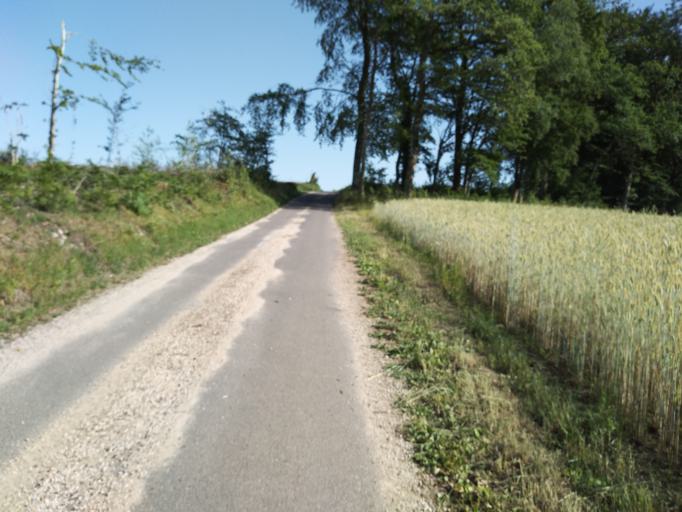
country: FR
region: Bourgogne
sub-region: Departement de la Cote-d'Or
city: Saulieu
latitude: 47.2822
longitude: 4.1500
